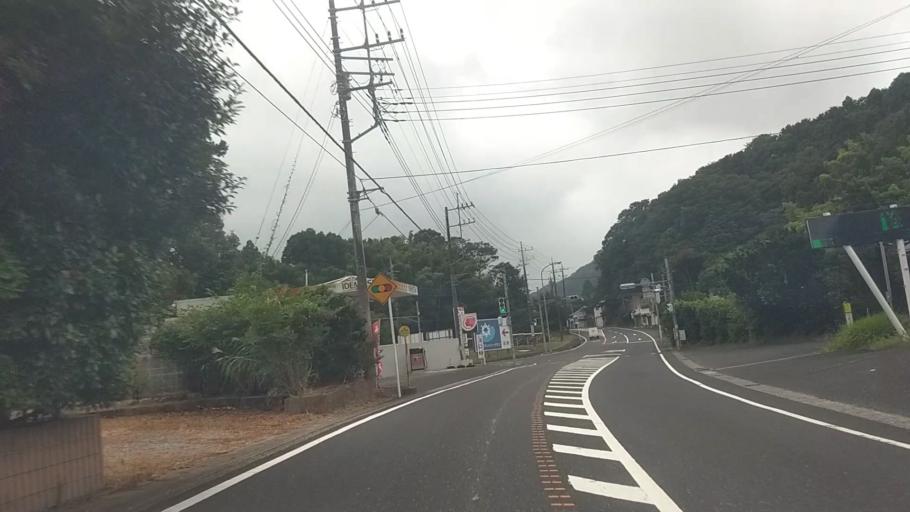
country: JP
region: Chiba
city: Kawaguchi
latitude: 35.2287
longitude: 140.0755
